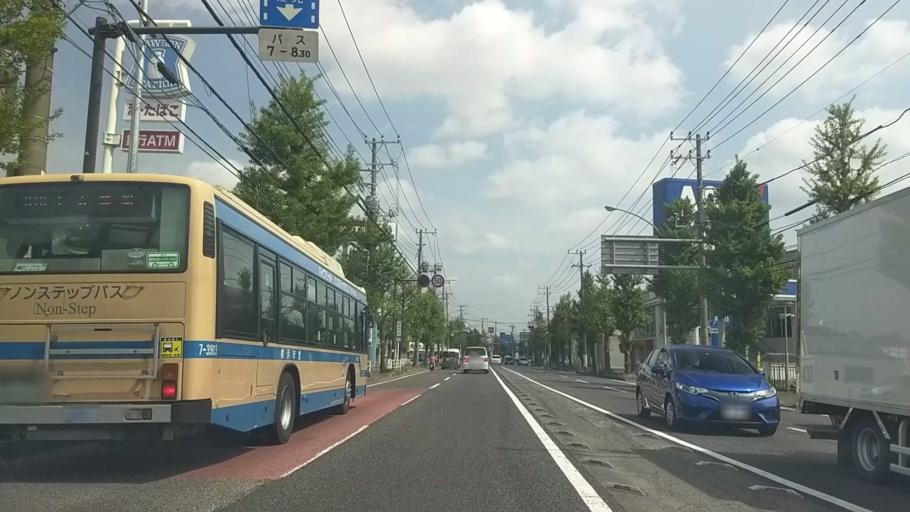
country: JP
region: Kanagawa
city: Yokohama
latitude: 35.3903
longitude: 139.5825
